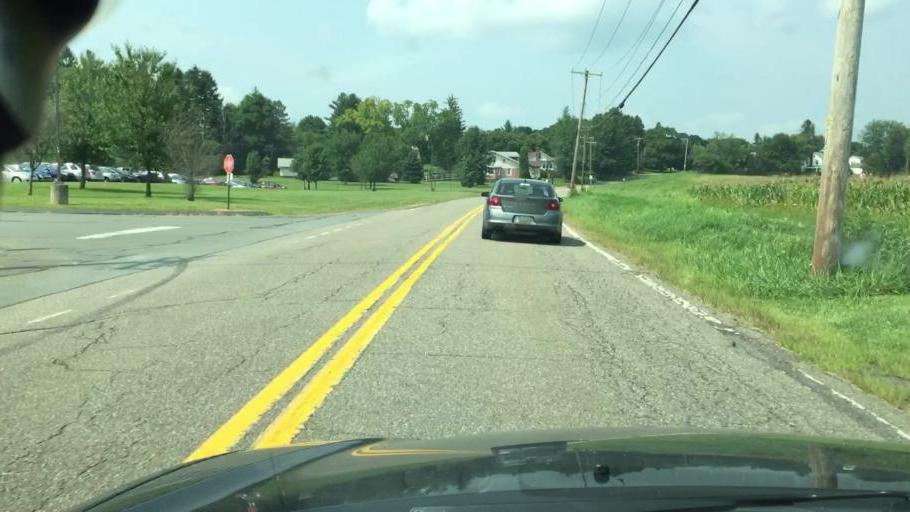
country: US
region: Pennsylvania
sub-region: Luzerne County
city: Harleigh
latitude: 41.0104
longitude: -75.9998
